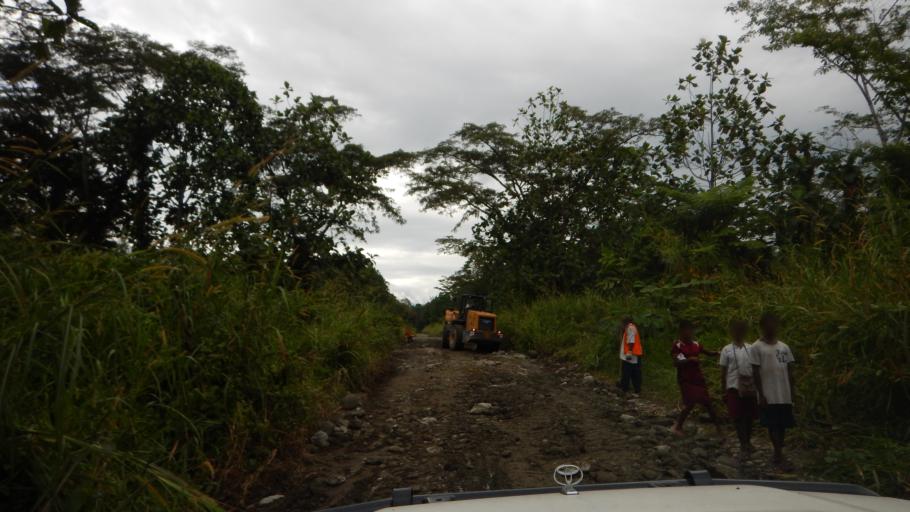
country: PG
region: Northern Province
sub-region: Sohe
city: Kokoda
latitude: -8.9186
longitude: 147.8953
